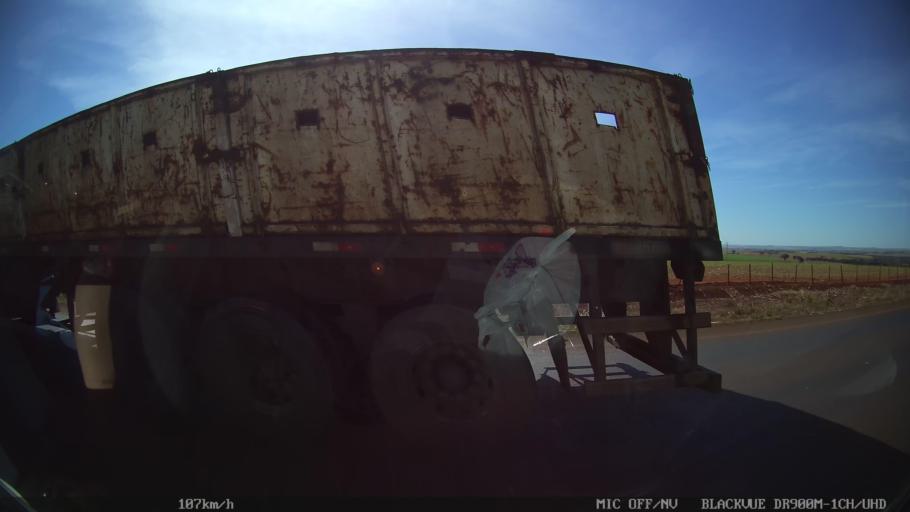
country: BR
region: Sao Paulo
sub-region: Sao Joaquim Da Barra
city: Sao Joaquim da Barra
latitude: -20.5120
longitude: -47.9019
